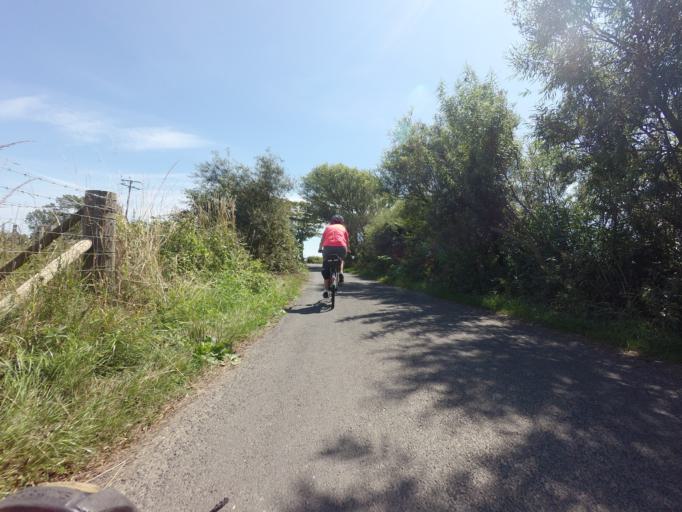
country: GB
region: England
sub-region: Kent
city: Lydd
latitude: 50.9878
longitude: 0.8946
